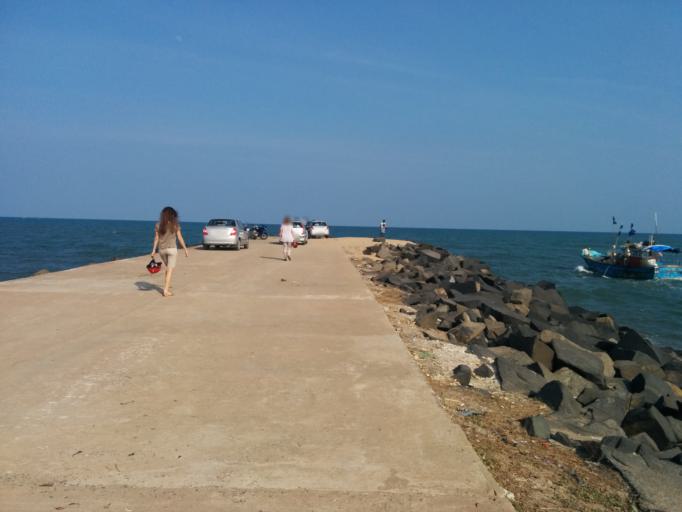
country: IN
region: Pondicherry
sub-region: Puducherry
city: Puducherry
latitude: 11.9073
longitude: 79.8304
